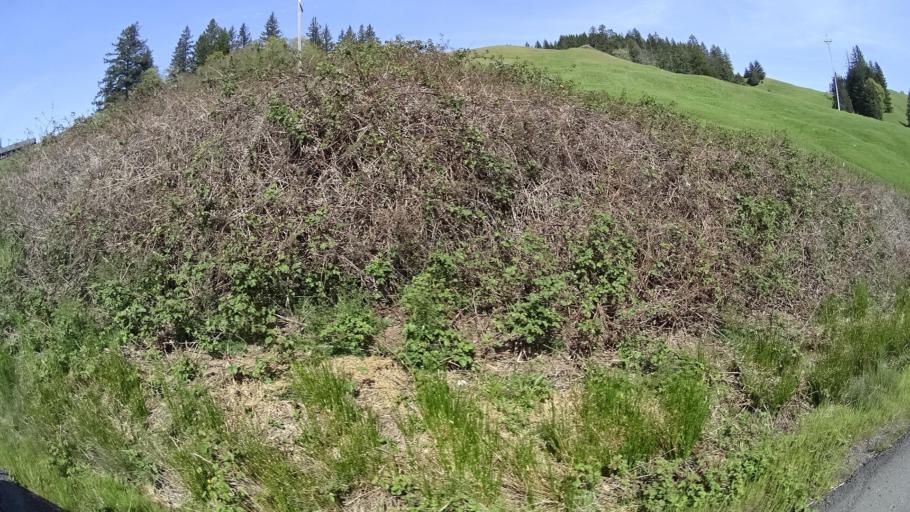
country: US
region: California
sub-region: Humboldt County
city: Redway
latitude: 40.4127
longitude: -123.7576
